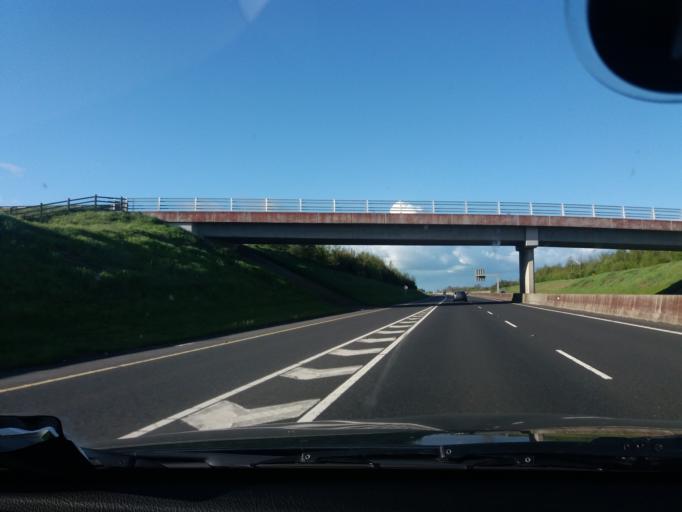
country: IE
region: Leinster
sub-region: County Carlow
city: Bagenalstown
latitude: 52.6842
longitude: -7.0344
